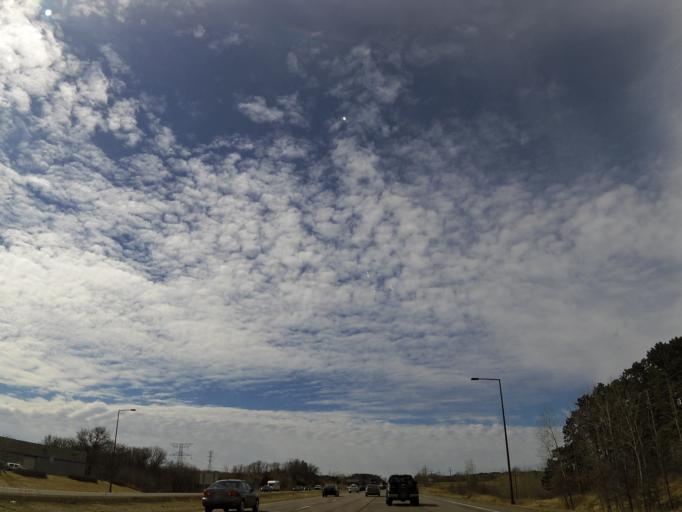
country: US
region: Minnesota
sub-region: Washington County
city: Lake Elmo
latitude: 45.0363
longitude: -92.8521
